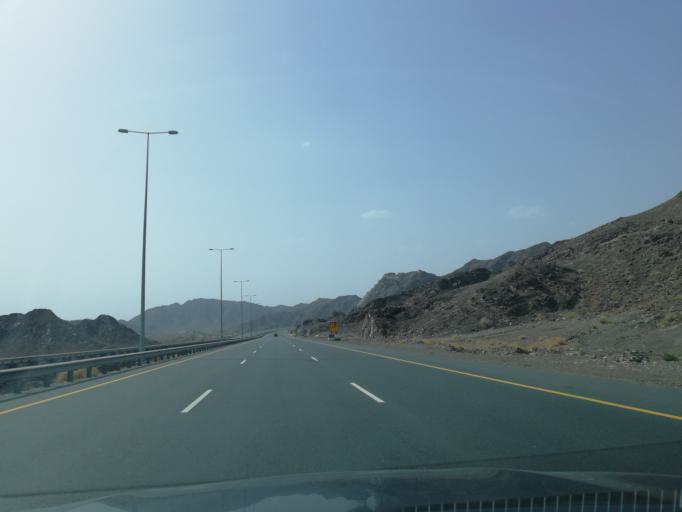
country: OM
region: Muhafazat ad Dakhiliyah
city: Sufalat Sama'il
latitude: 22.9738
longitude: 58.2378
